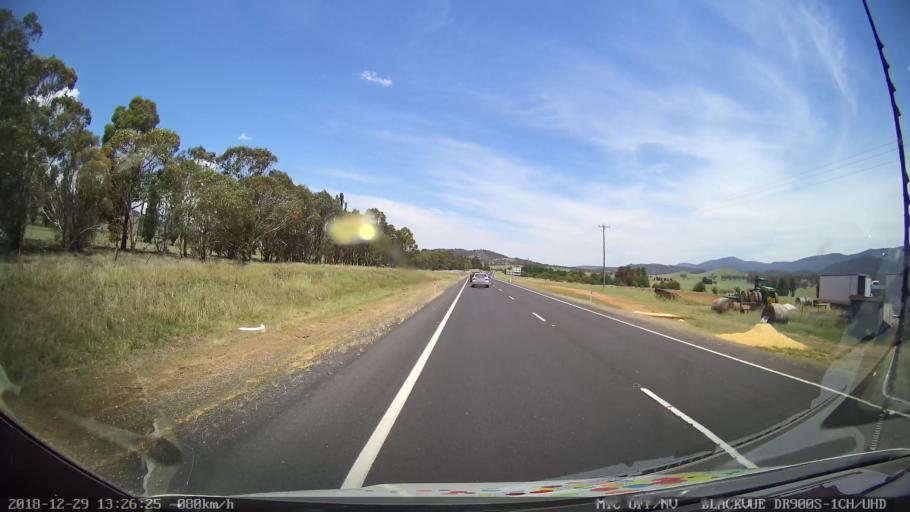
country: AU
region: New South Wales
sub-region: Cooma-Monaro
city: Cooma
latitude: -35.8552
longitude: 149.1591
